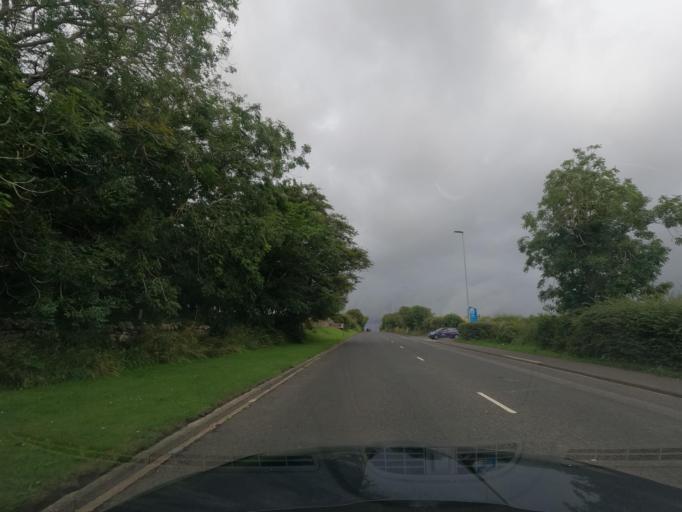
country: GB
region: England
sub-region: Northumberland
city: Berwick-Upon-Tweed
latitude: 55.7477
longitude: -1.9994
